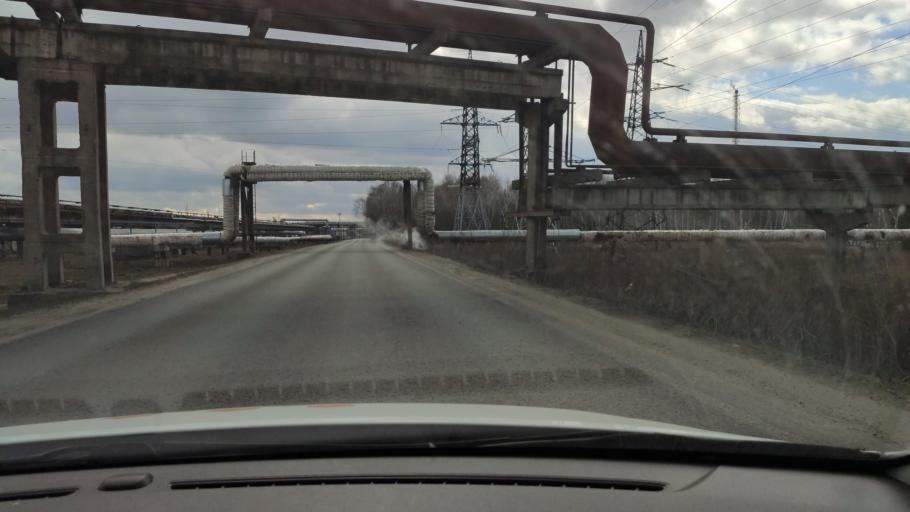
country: RU
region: Tatarstan
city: Staroye Arakchino
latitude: 55.8683
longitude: 48.9731
